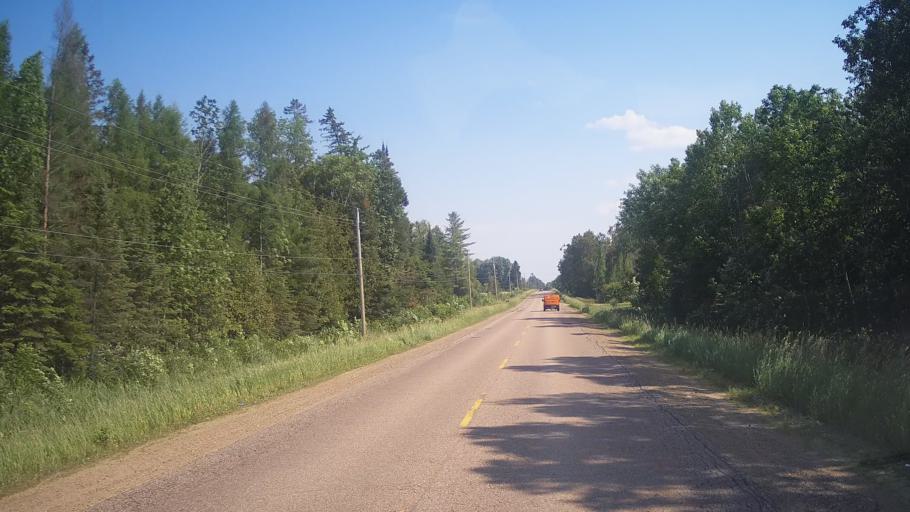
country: CA
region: Ontario
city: Pembroke
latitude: 45.5961
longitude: -77.2308
